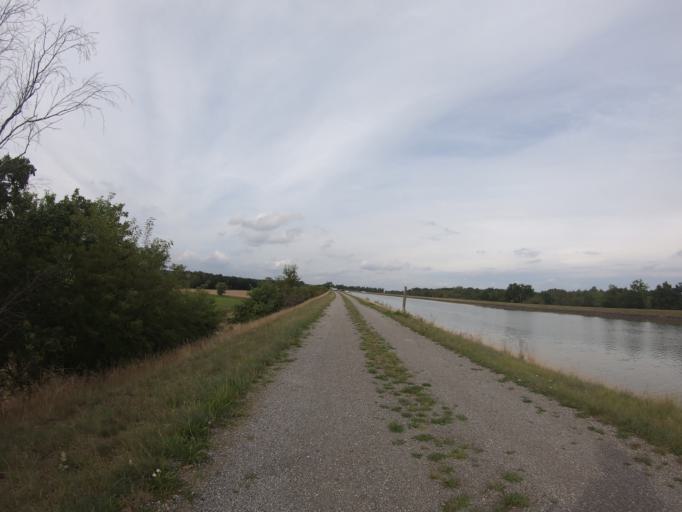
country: DE
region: Lower Saxony
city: Osloss
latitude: 52.4699
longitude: 10.6597
